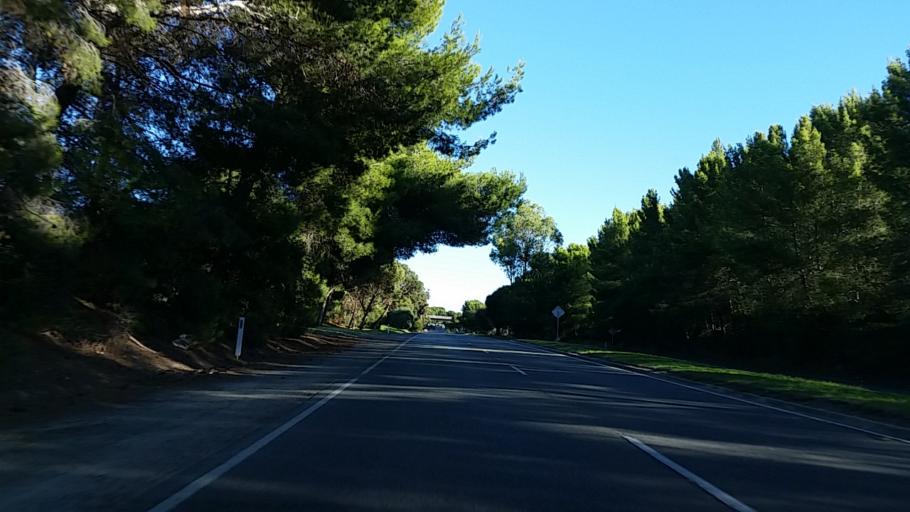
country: AU
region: South Australia
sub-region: Onkaparinga
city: Reynella
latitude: -35.0905
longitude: 138.5374
